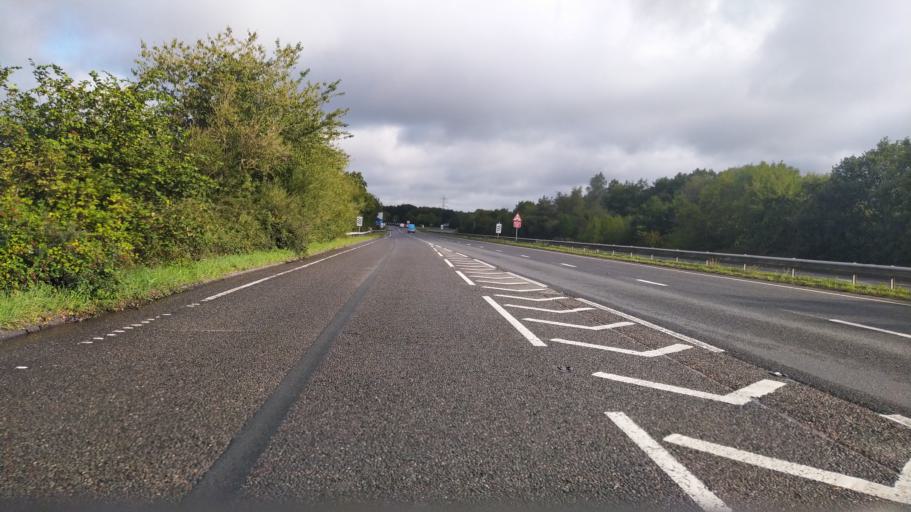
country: GB
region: England
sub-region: Hampshire
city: Totton
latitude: 50.9418
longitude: -1.5287
